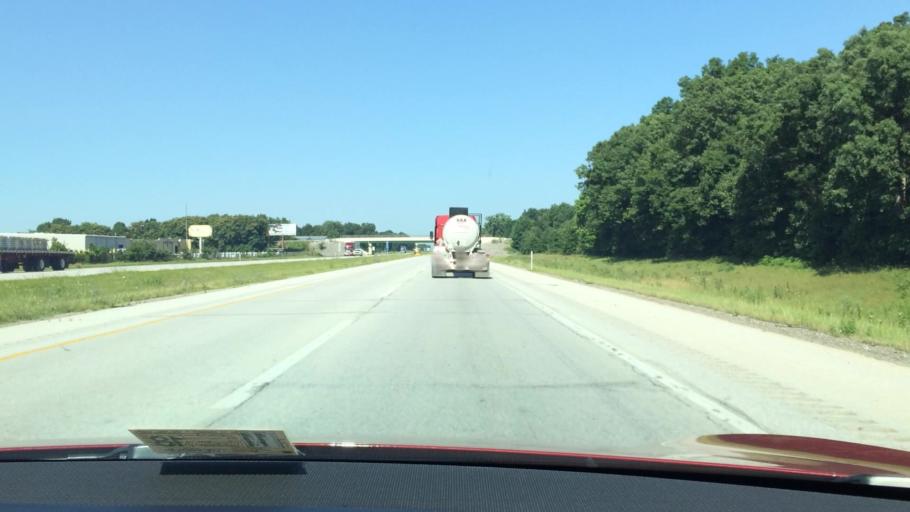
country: US
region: Indiana
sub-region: Elkhart County
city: Simonton Lake
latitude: 41.7298
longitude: -85.9230
